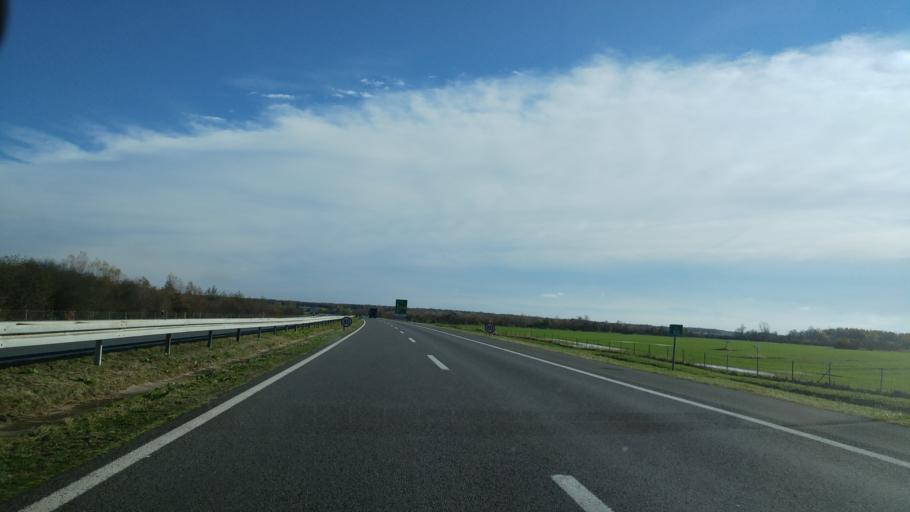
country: HR
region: Brodsko-Posavska
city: Okucani
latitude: 45.2358
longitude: 17.1969
